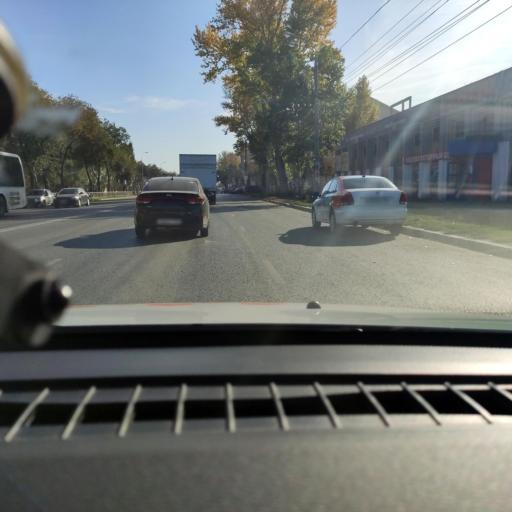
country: RU
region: Samara
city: Samara
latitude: 53.1958
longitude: 50.1905
